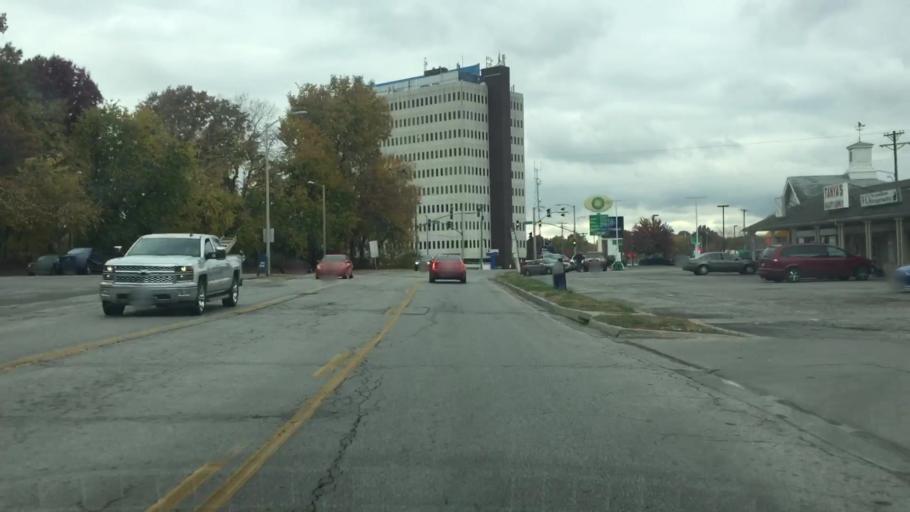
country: US
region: Missouri
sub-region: Jackson County
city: Raytown
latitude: 39.0429
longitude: -94.4378
